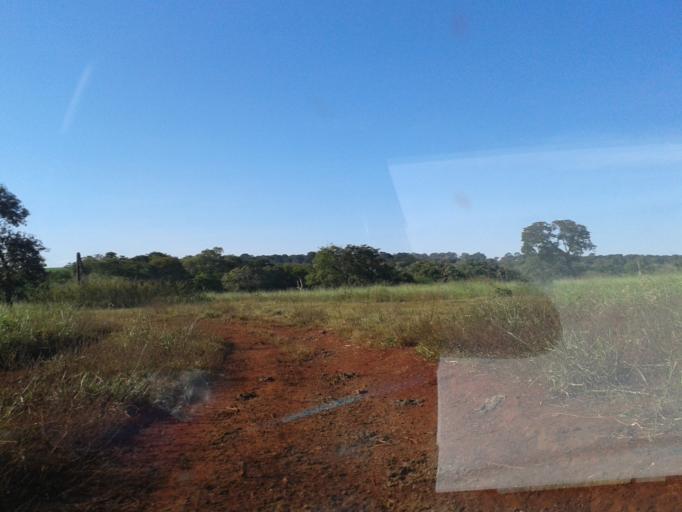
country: BR
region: Minas Gerais
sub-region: Santa Vitoria
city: Santa Vitoria
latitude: -18.9935
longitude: -50.3506
